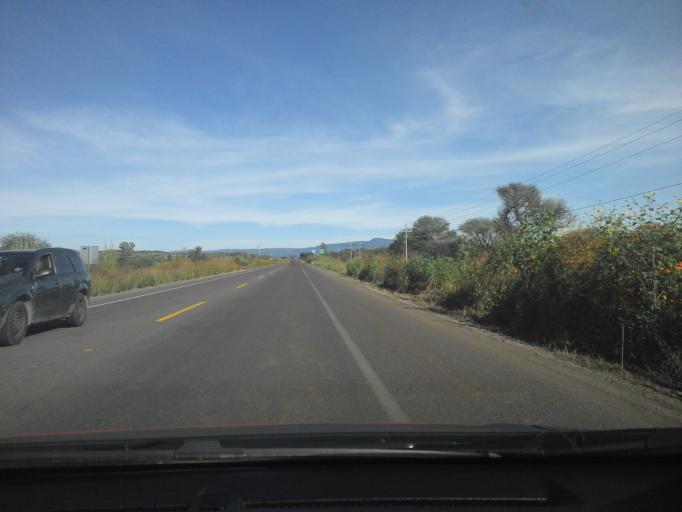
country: MX
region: Jalisco
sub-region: Teuchitlan
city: La Estanzuela
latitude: 20.6720
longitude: -103.8173
